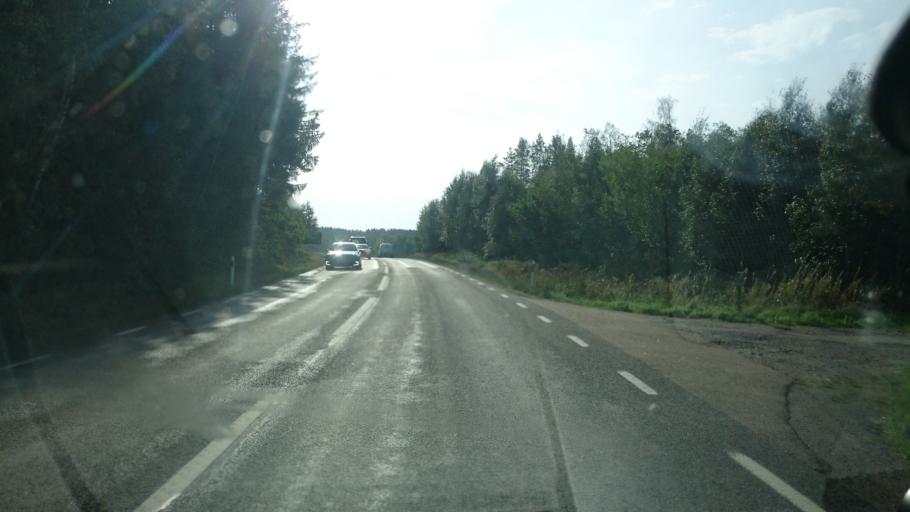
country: SE
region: Vaestra Goetaland
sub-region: Vanersborgs Kommun
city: Vargon
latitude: 58.2606
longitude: 12.4022
